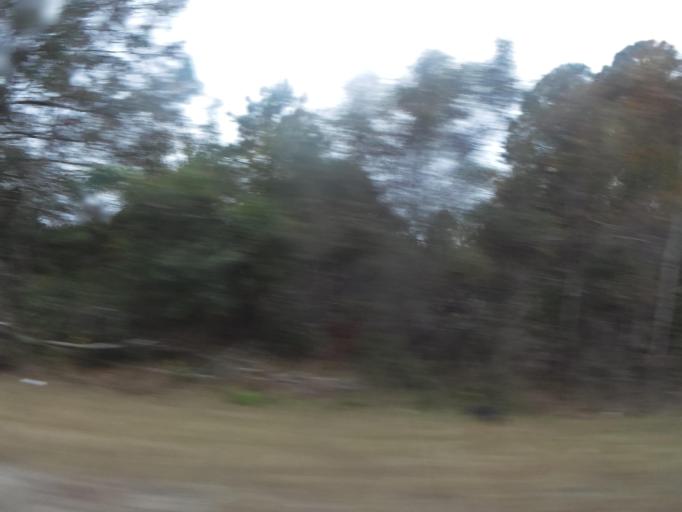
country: US
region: Georgia
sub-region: Charlton County
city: Folkston
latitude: 30.9121
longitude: -82.0780
